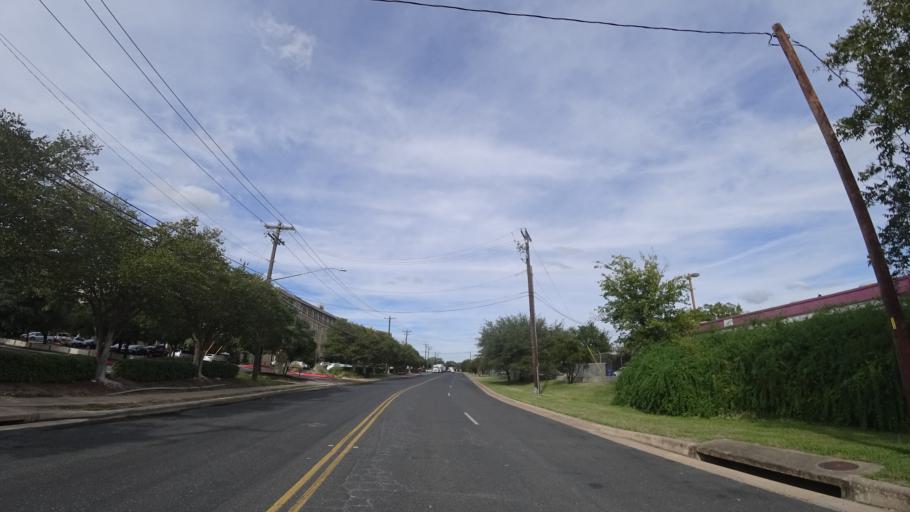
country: US
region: Texas
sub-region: Travis County
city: Austin
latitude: 30.2098
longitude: -97.7533
